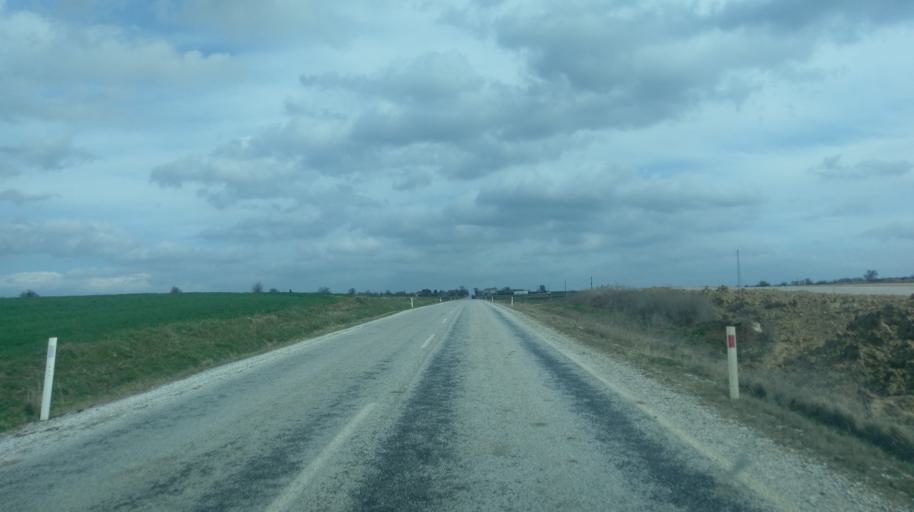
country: TR
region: Kirklareli
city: Inece
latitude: 41.6687
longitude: 26.9722
